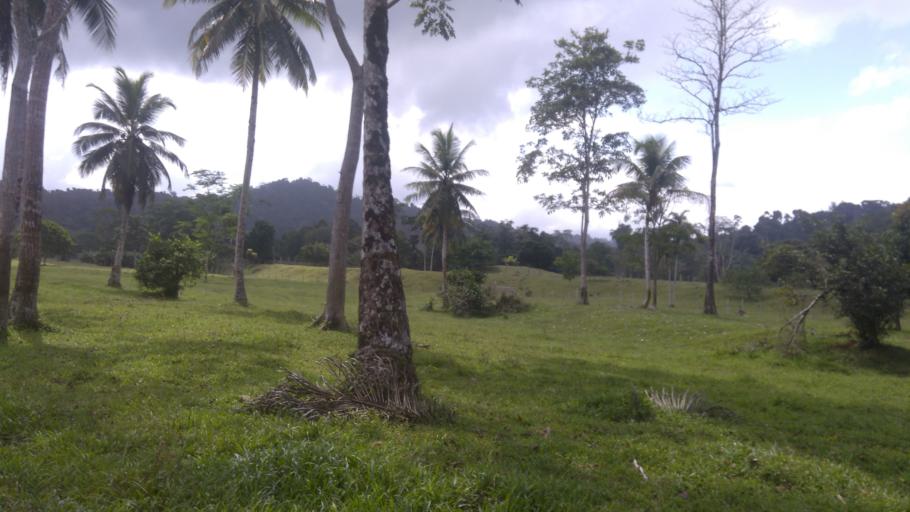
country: PA
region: Guna Yala
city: Puerto Obaldia
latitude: 8.6126
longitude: -77.3865
